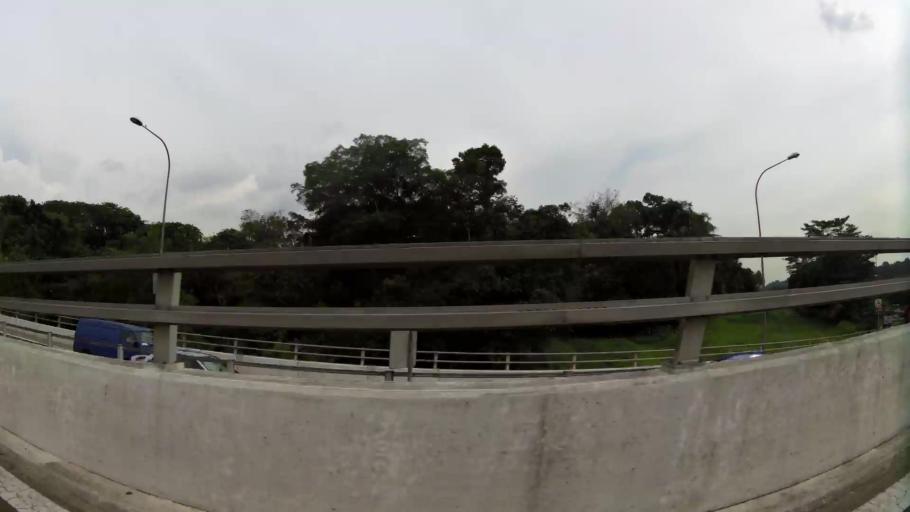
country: MY
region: Johor
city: Johor Bahru
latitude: 1.4200
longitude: 103.7718
